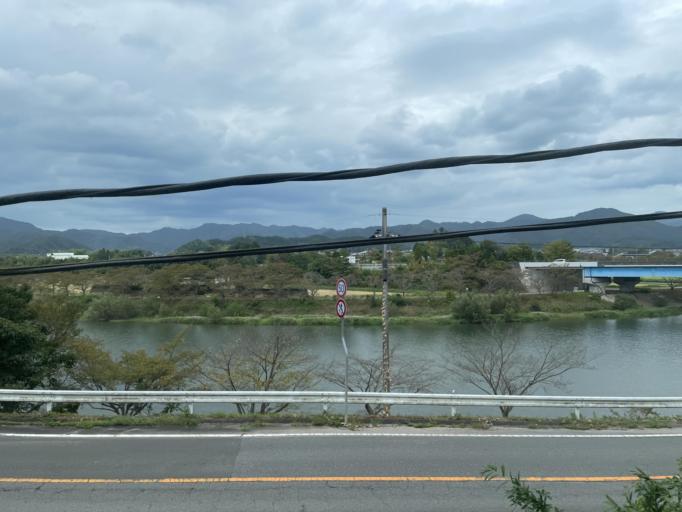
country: JP
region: Hyogo
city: Sasayama
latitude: 35.0701
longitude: 135.1728
